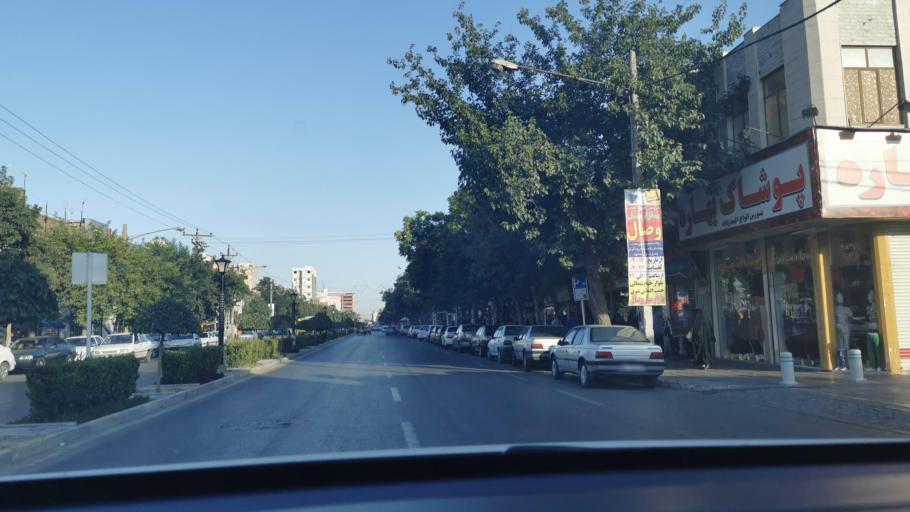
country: IR
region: Razavi Khorasan
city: Mashhad
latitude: 36.2968
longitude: 59.6427
